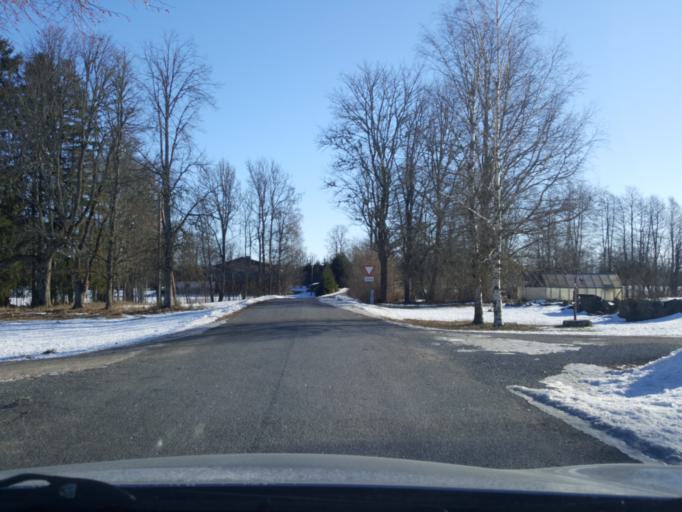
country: EE
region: Viljandimaa
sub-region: Viljandi linn
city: Viljandi
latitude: 58.4610
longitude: 25.5864
